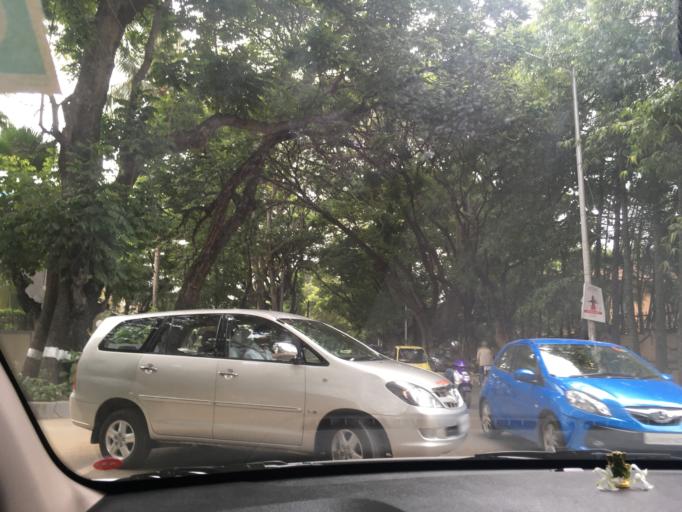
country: IN
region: Karnataka
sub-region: Bangalore Urban
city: Bangalore
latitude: 12.9304
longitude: 77.6275
